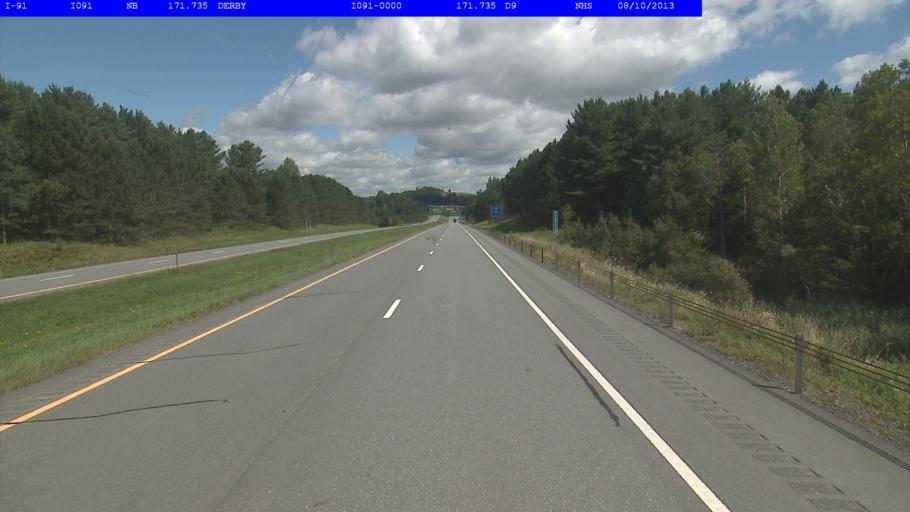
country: US
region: Vermont
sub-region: Orleans County
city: Newport
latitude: 44.9438
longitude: -72.1569
